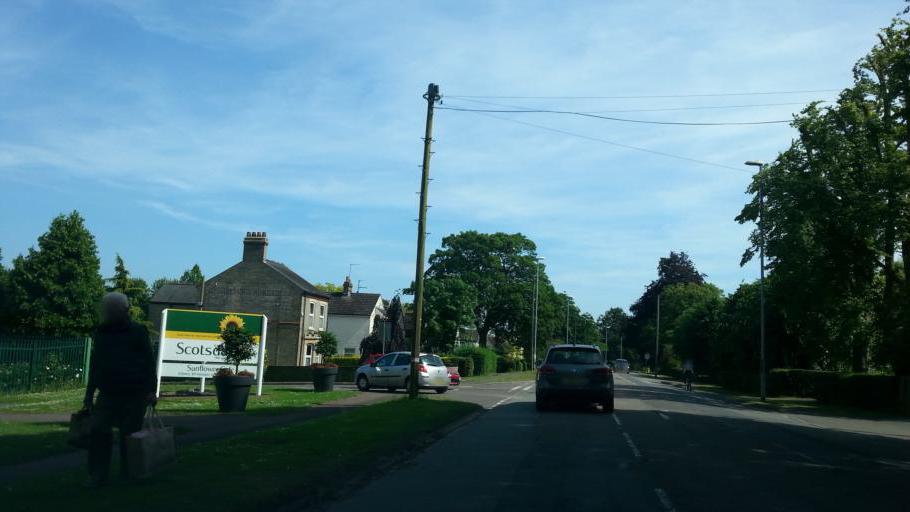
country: GB
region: England
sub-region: Cambridgeshire
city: Grantchester
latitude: 52.1603
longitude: 0.1257
